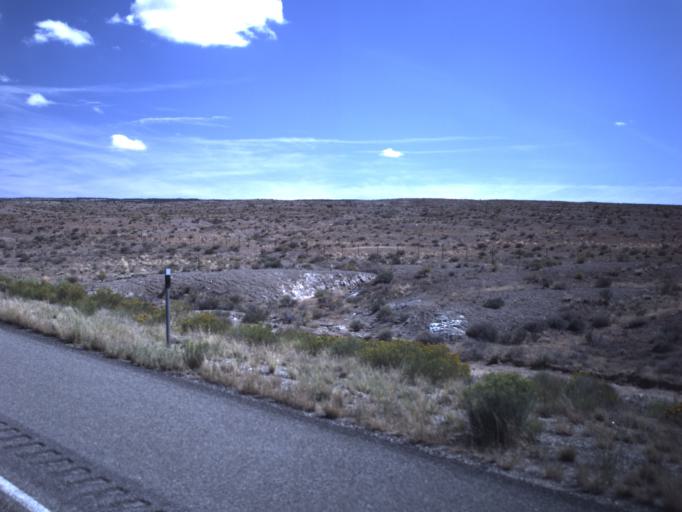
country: US
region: Utah
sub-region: Emery County
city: Ferron
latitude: 38.8468
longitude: -111.0025
